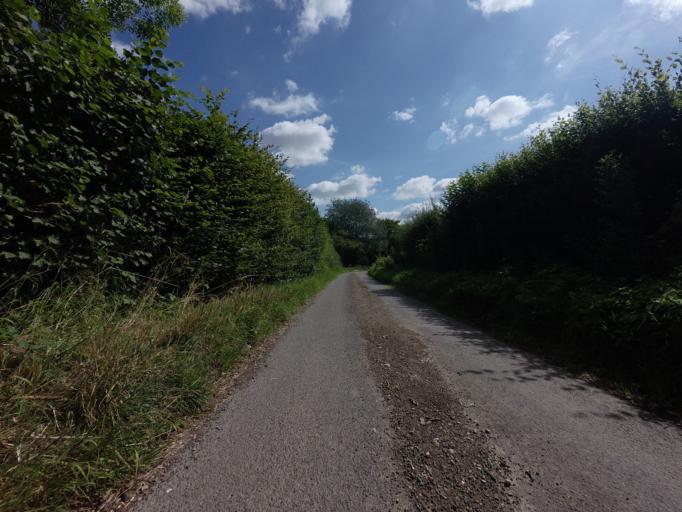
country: GB
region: England
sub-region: Kent
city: Tenterden
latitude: 51.0683
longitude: 0.7193
